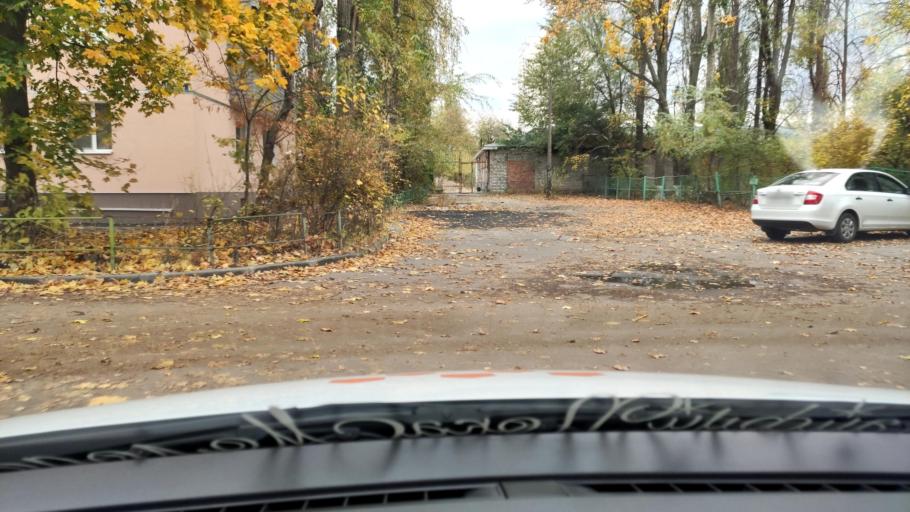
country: RU
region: Voronezj
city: Voronezh
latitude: 51.6580
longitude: 39.1511
